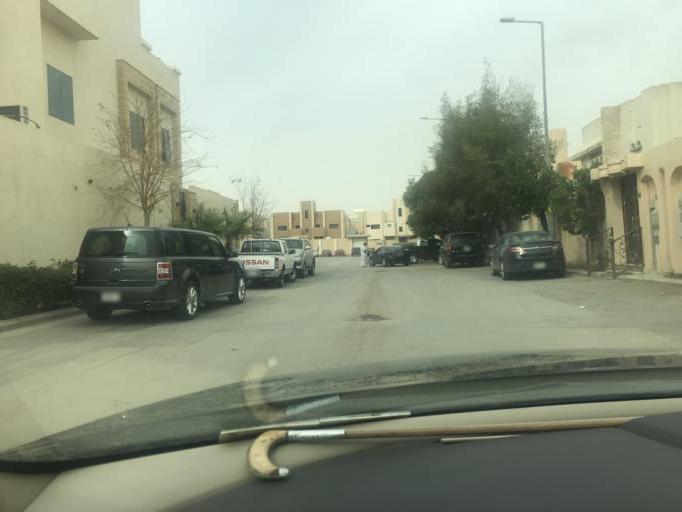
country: SA
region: Ar Riyad
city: Riyadh
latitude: 24.7542
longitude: 46.7669
